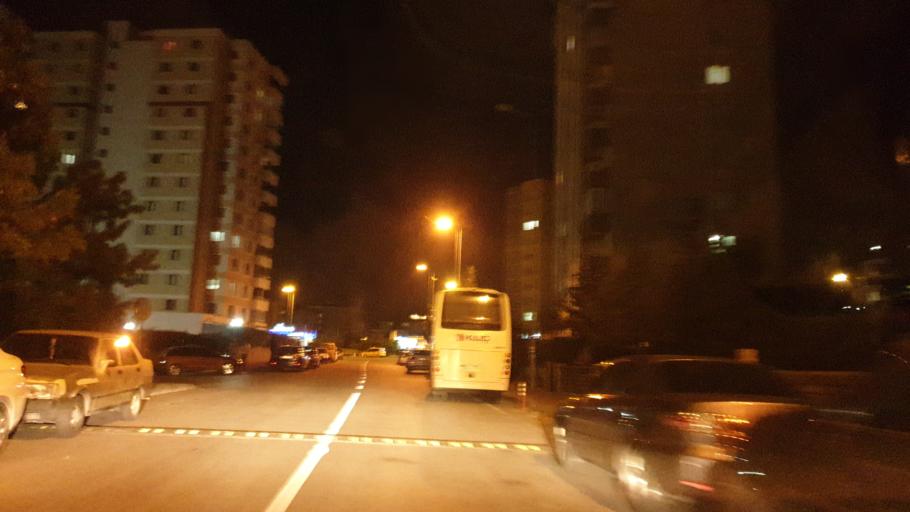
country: TR
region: Kayseri
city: Talas
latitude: 38.6930
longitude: 35.5439
